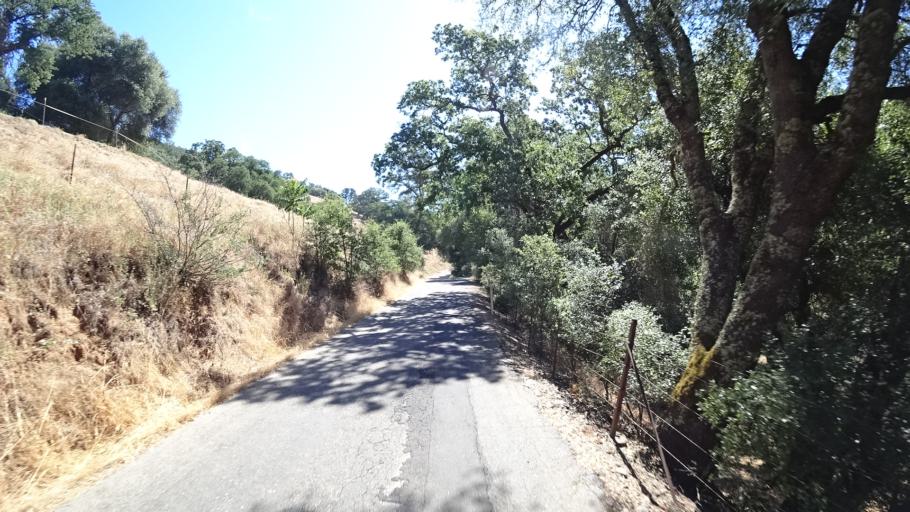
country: US
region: California
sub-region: Calaveras County
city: Angels Camp
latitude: 38.1469
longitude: -120.5801
